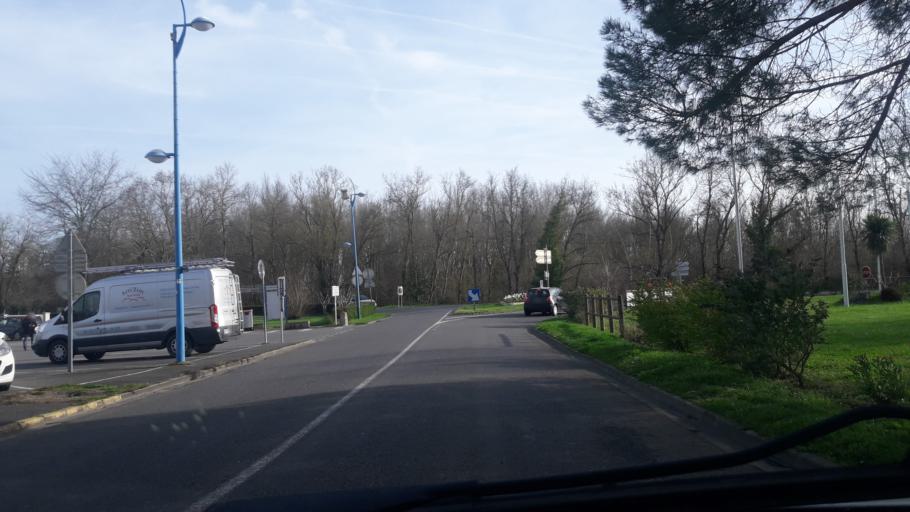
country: FR
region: Midi-Pyrenees
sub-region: Departement du Gers
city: Pujaudran
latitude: 43.6152
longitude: 1.0737
